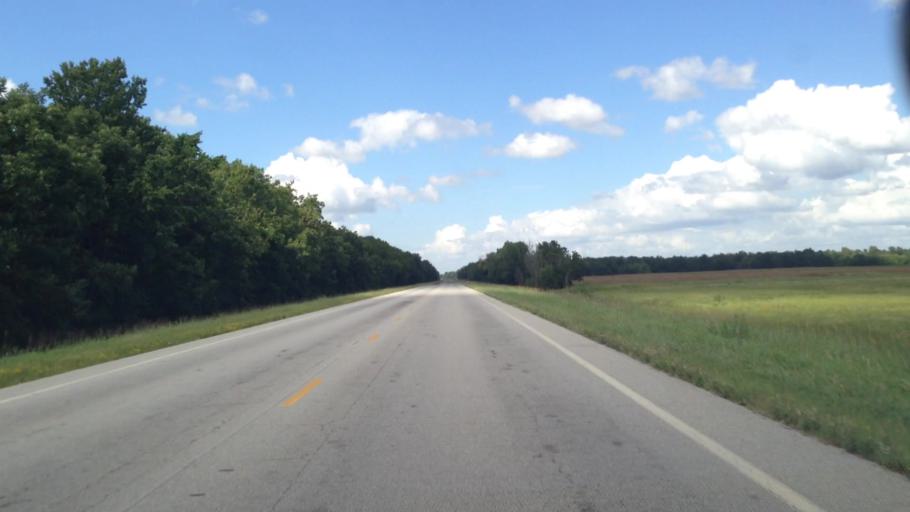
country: US
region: Kansas
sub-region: Labette County
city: Chetopa
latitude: 37.0639
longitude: -95.1027
